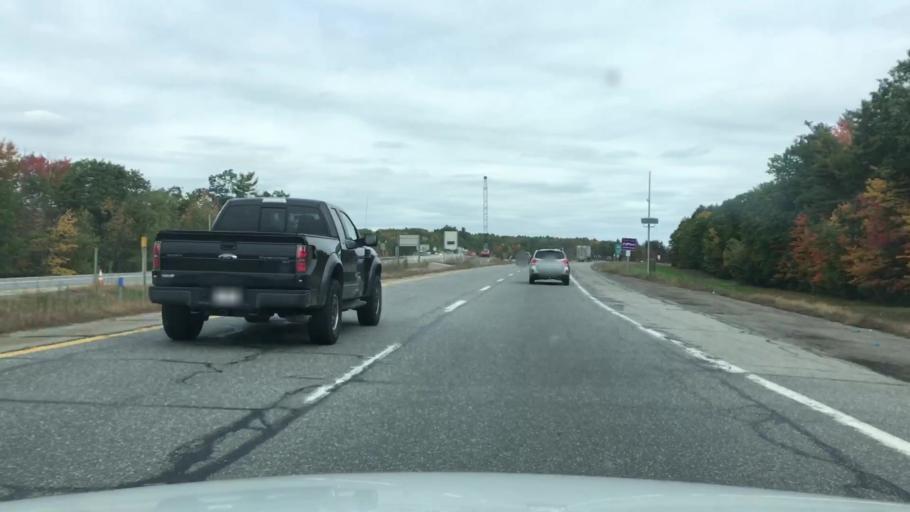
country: US
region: Maine
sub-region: Kennebec County
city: Gardiner
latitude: 44.2139
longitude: -69.8241
